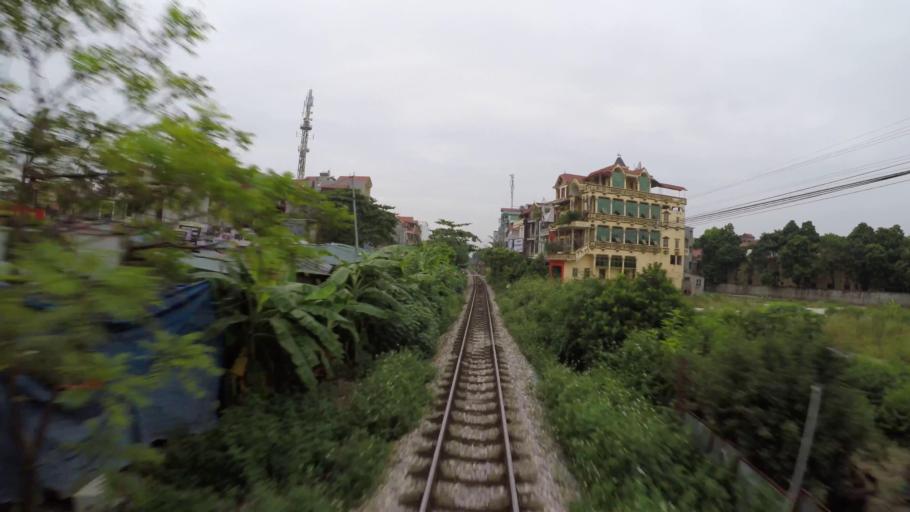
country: VN
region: Hung Yen
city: Nhu Quynh
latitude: 20.9779
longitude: 106.0127
